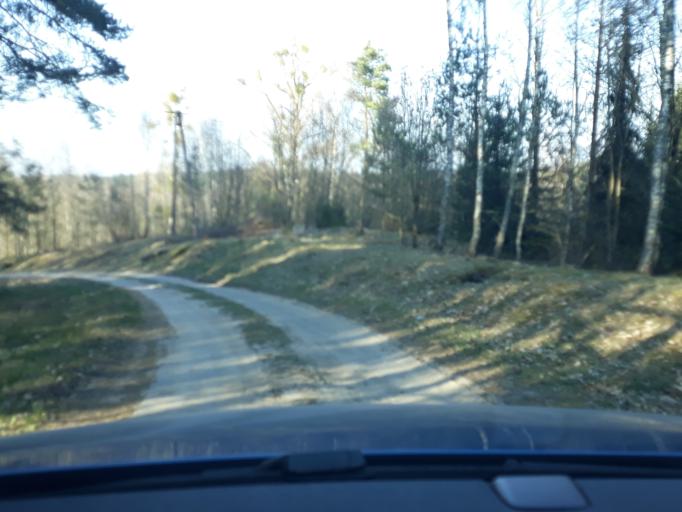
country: PL
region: Pomeranian Voivodeship
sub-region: Powiat bytowski
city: Lipnica
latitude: 53.9238
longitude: 17.4469
